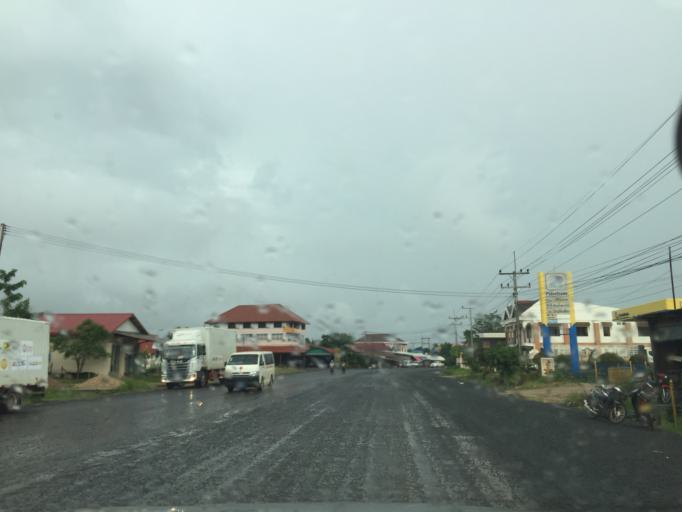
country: LA
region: Attapu
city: Attapu
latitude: 14.8227
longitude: 106.8111
